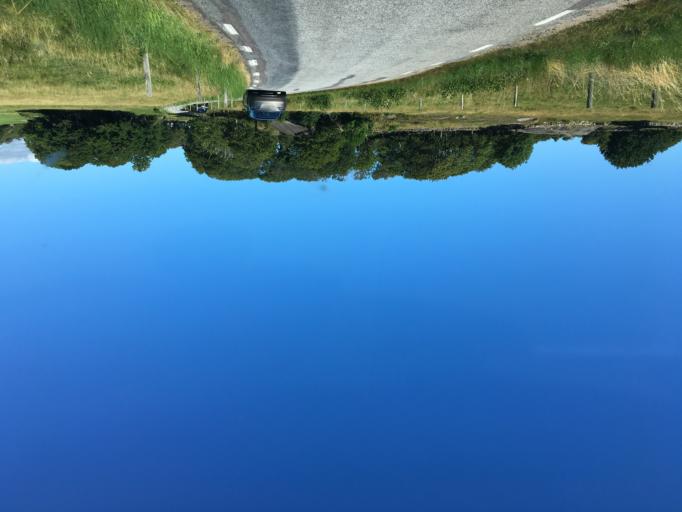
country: SE
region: Vaestra Goetaland
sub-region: Sotenas Kommun
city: Hunnebostrand
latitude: 58.4250
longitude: 11.2655
